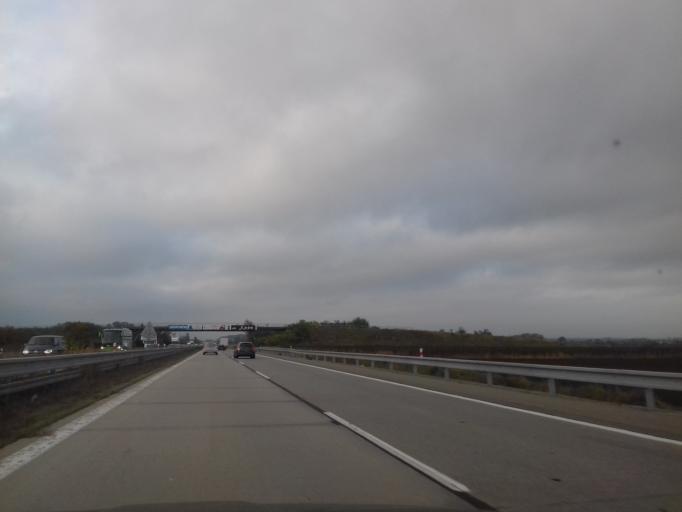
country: CZ
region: South Moravian
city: Rajhradice
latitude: 49.0837
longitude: 16.6588
